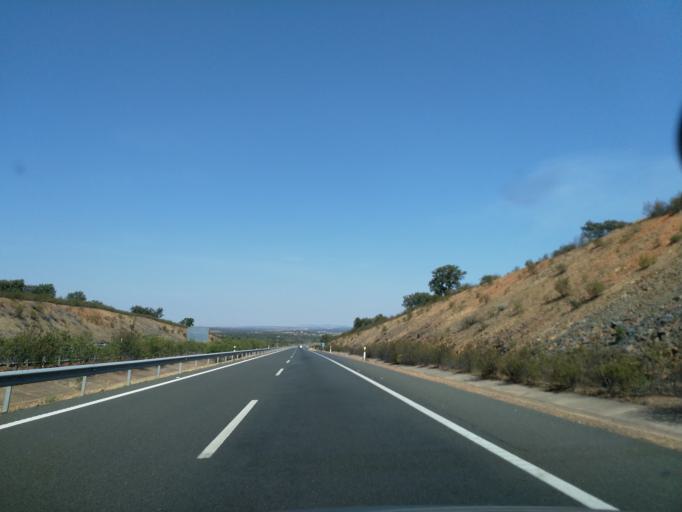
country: ES
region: Extremadura
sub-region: Provincia de Caceres
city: Alcuescar
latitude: 39.1770
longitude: -6.2722
